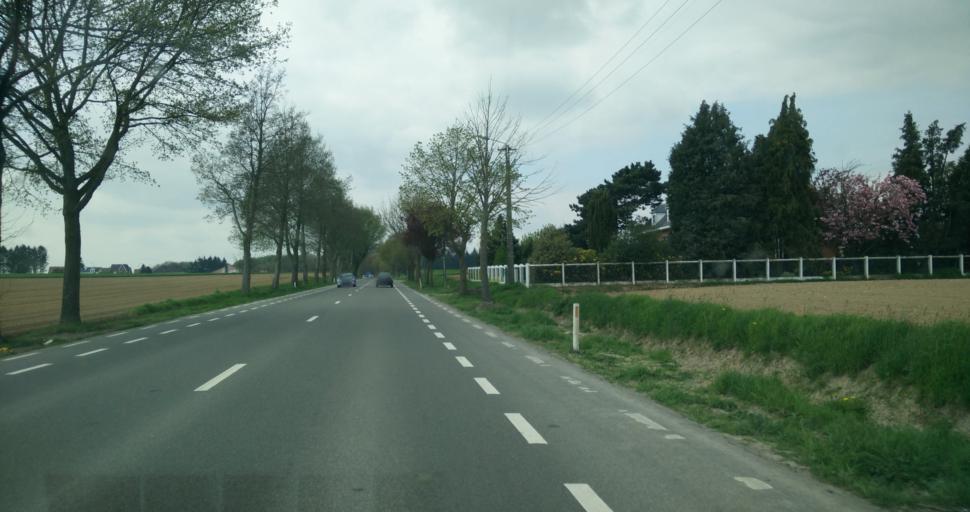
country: BE
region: Wallonia
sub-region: Province du Brabant Wallon
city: Tubize
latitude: 50.6536
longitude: 4.1711
